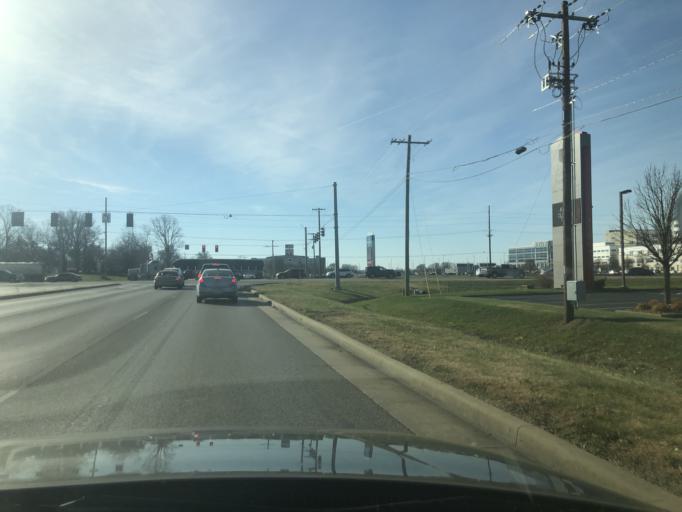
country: US
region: Indiana
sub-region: Warrick County
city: Newburgh
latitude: 37.9776
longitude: -87.4413
